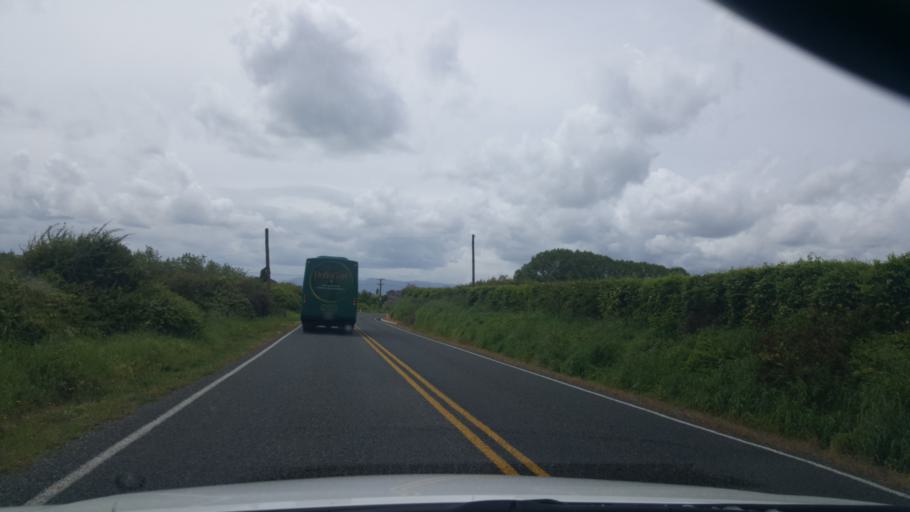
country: NZ
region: Waikato
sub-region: Matamata-Piako District
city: Matamata
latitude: -37.8785
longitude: 175.6985
